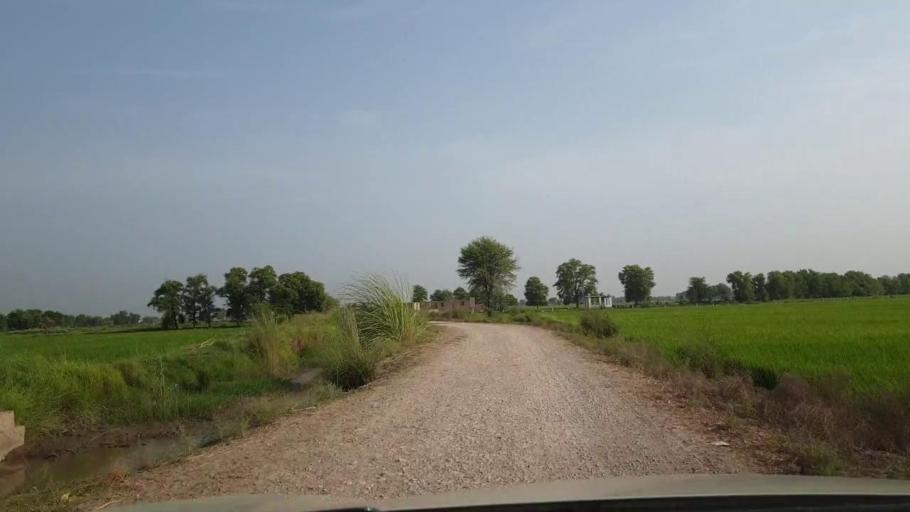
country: PK
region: Sindh
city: Larkana
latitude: 27.4907
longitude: 68.2067
